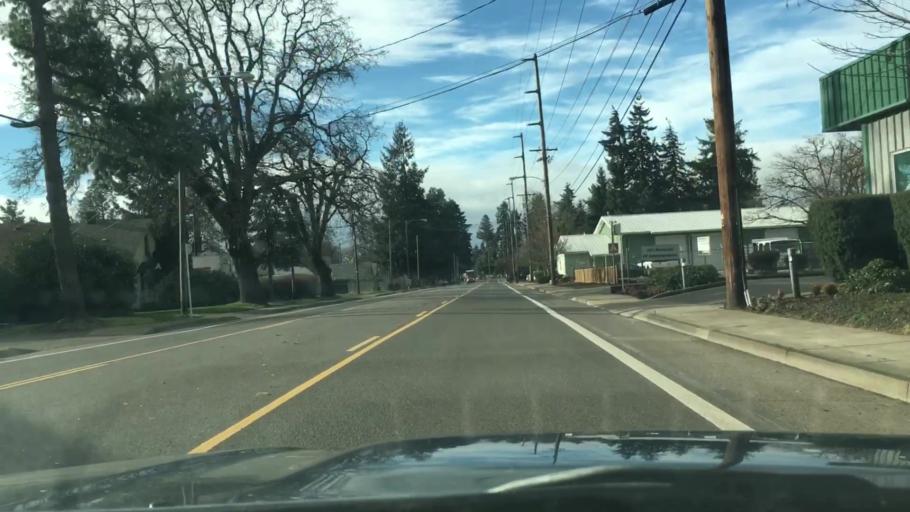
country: US
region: Oregon
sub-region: Lane County
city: Eugene
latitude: 44.0634
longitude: -123.1246
